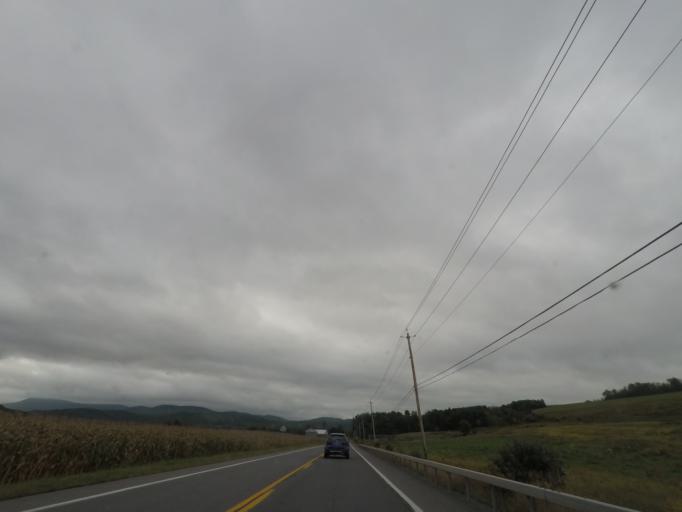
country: US
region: New York
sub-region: Rensselaer County
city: Hoosick Falls
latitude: 42.8711
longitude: -73.3526
